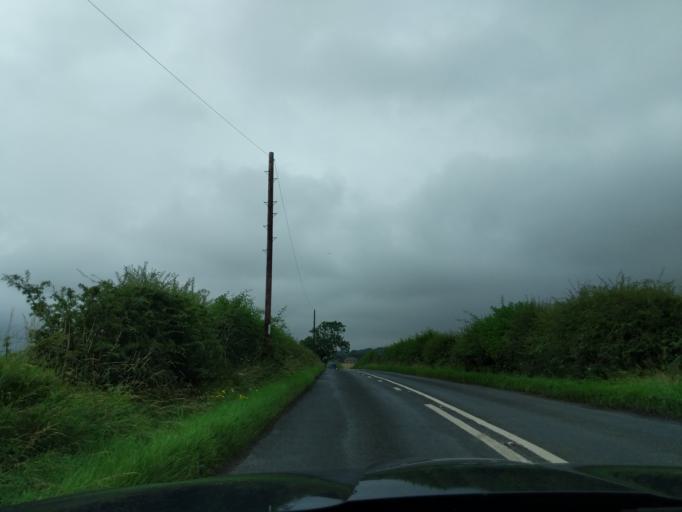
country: GB
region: England
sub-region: Northumberland
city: Ford
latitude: 55.6633
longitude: -2.1016
